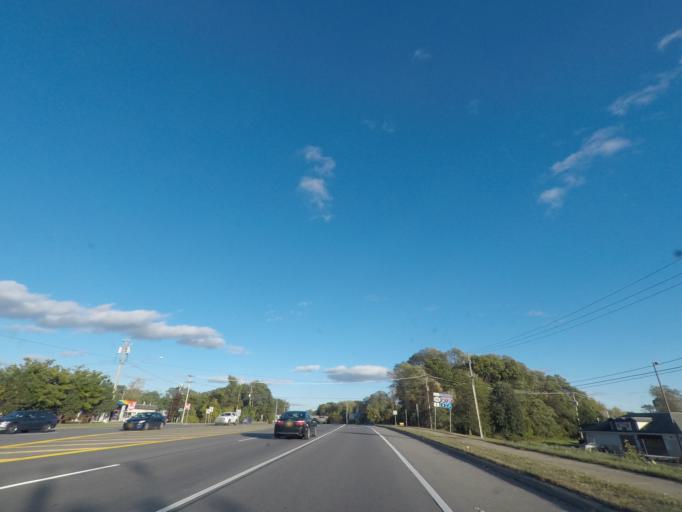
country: US
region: New York
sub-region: Saratoga County
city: Country Knolls
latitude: 42.8626
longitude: -73.7795
